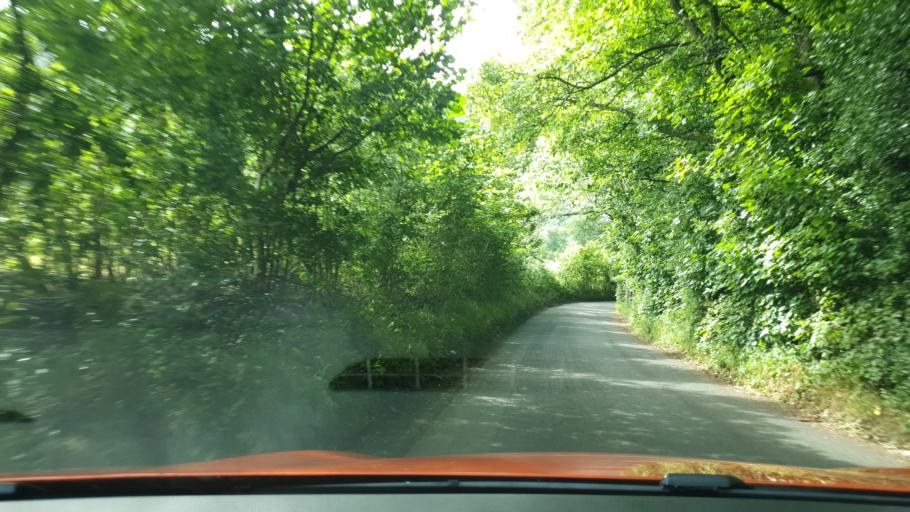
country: GB
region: England
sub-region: Cumbria
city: Penrith
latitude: 54.5908
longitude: -2.8418
